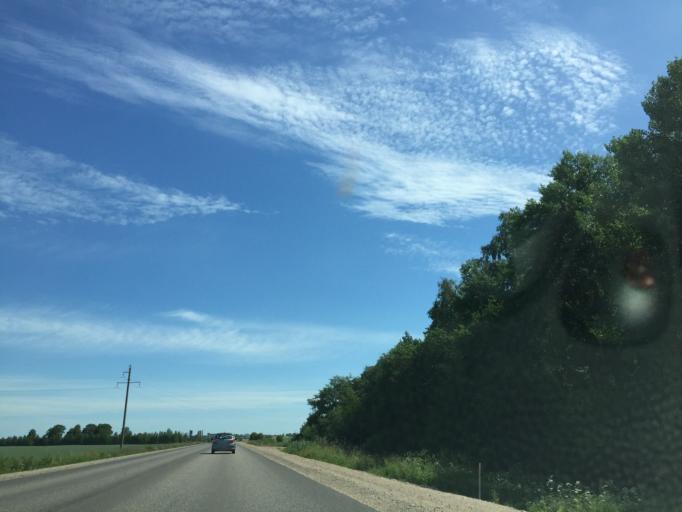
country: LV
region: Saldus Rajons
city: Saldus
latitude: 56.6729
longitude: 22.4344
